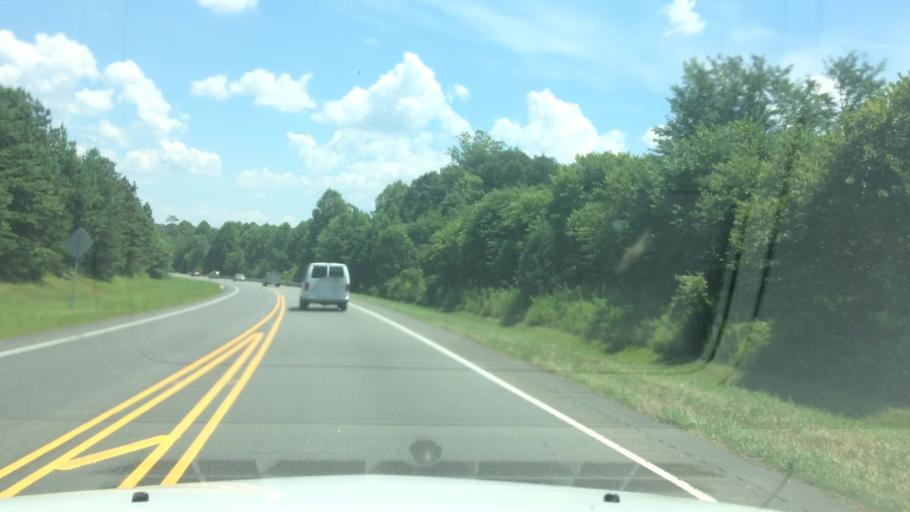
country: US
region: North Carolina
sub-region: Alexander County
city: Stony Point
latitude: 35.8164
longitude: -80.9993
